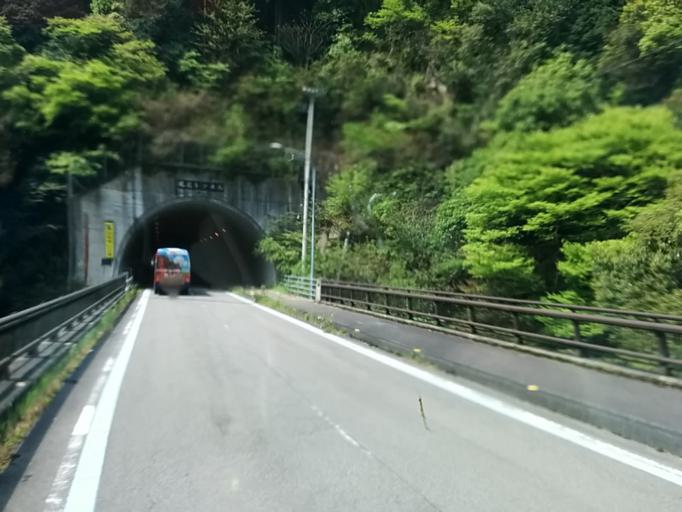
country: JP
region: Ehime
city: Niihama
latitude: 33.8882
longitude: 133.3064
